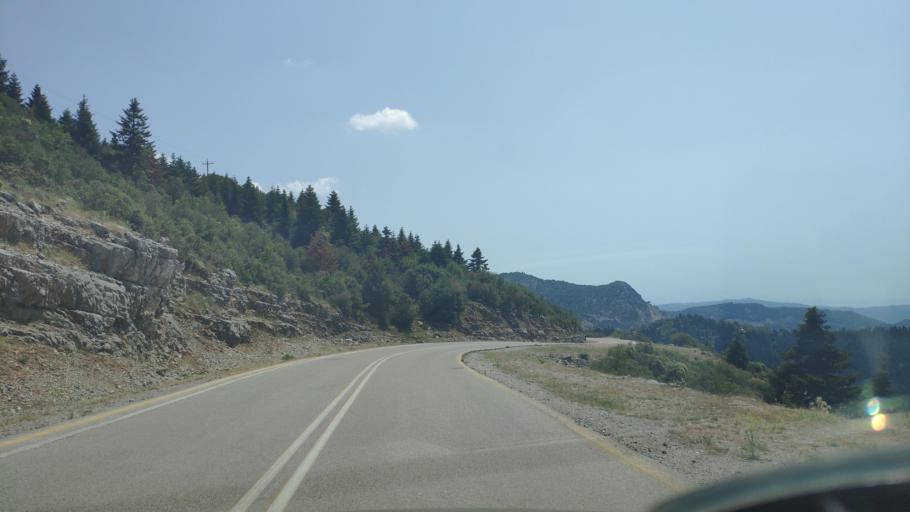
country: GR
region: Epirus
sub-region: Nomos Artas
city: Ano Kalentini
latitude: 39.2648
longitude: 21.2510
